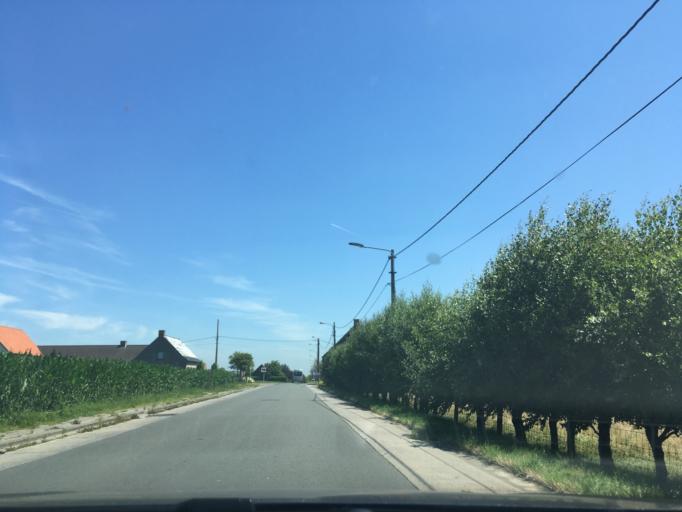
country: BE
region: Flanders
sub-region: Provincie West-Vlaanderen
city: Pittem
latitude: 51.0133
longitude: 3.2473
